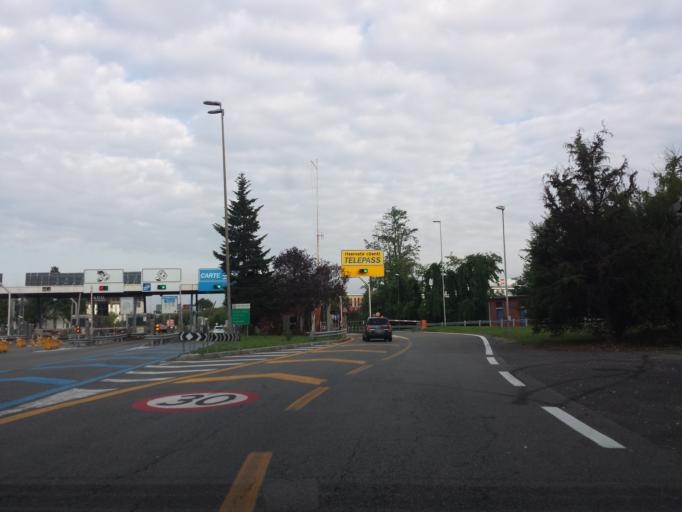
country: IT
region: Lombardy
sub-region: Citta metropolitana di Milano
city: Lainate
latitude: 45.5615
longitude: 9.0315
